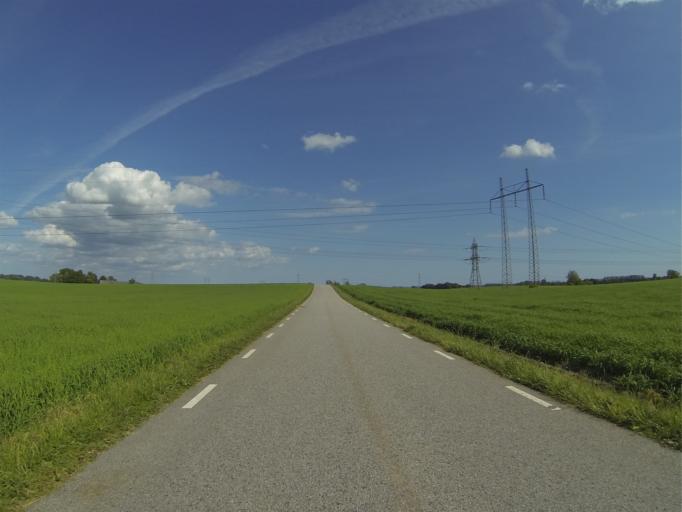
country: SE
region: Skane
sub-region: Staffanstorps Kommun
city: Hjaerup
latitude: 55.6358
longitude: 13.1213
